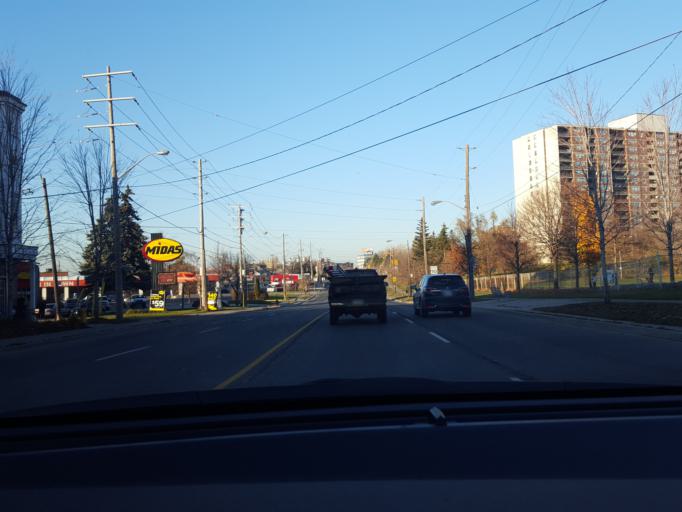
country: CA
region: Ontario
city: Scarborough
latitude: 43.7165
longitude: -79.3047
